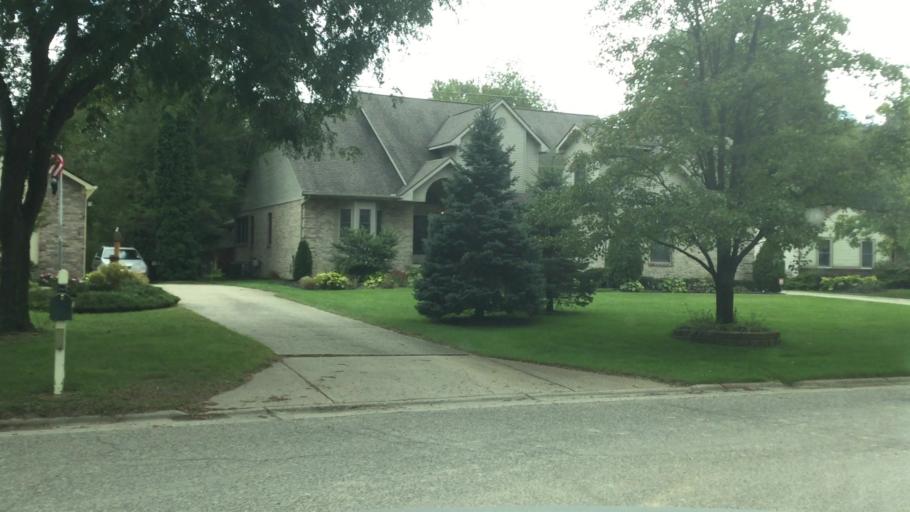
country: US
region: Michigan
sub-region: Livingston County
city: Brighton
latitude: 42.5592
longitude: -83.7438
